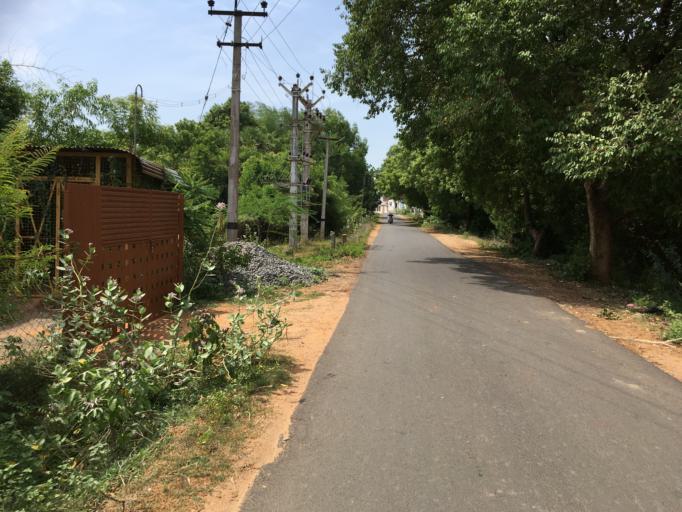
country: IN
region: Tamil Nadu
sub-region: Villupuram
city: Auroville
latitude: 12.0066
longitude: 79.7967
